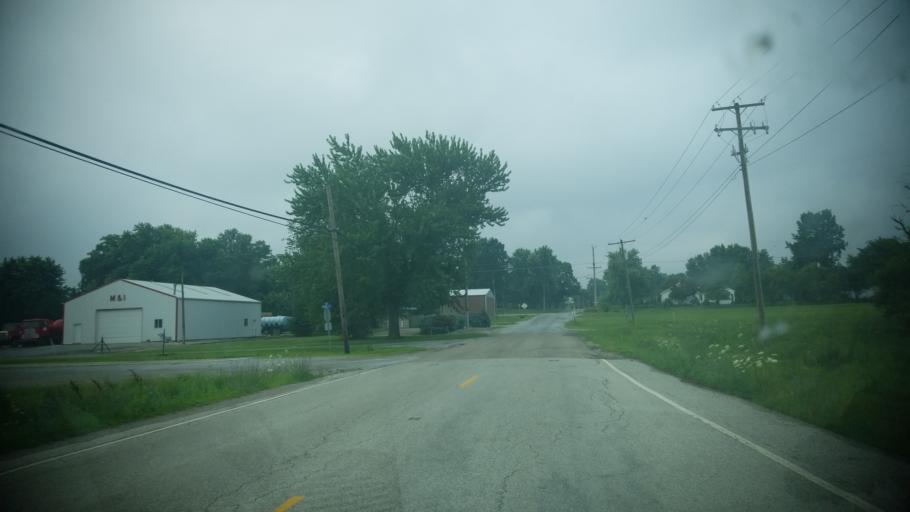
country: US
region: Illinois
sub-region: Clay County
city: Flora
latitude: 38.6793
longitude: -88.3541
